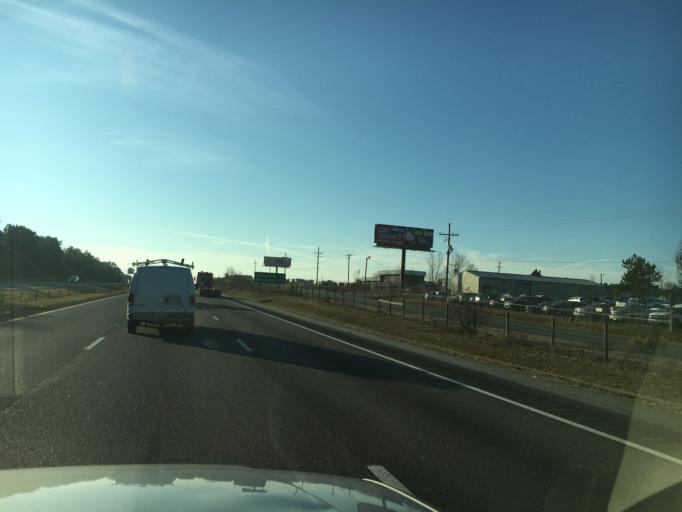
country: US
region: South Carolina
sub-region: Lexington County
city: Pineridge
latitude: 33.8687
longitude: -81.0338
